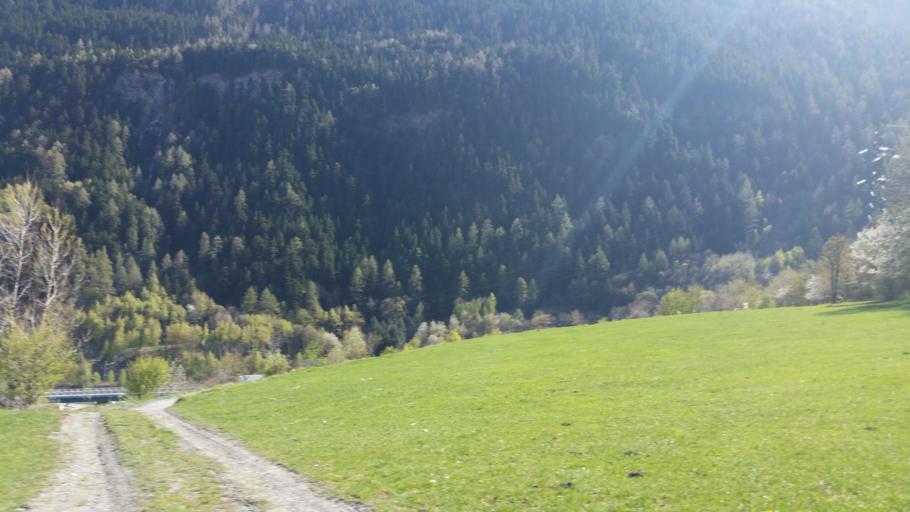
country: FR
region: Rhone-Alpes
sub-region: Departement de la Savoie
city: Modane
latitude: 45.1990
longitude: 6.6209
